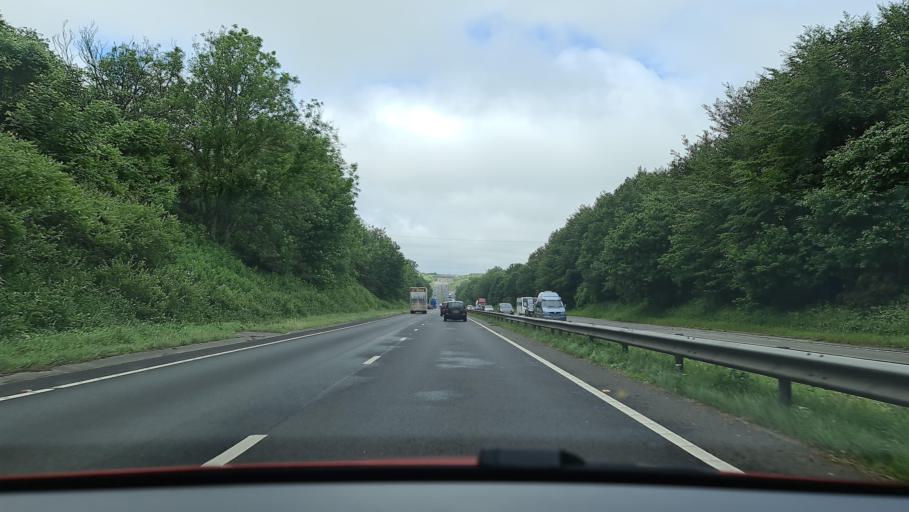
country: GB
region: England
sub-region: Cornwall
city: Bodmin
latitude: 50.4378
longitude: -4.7580
